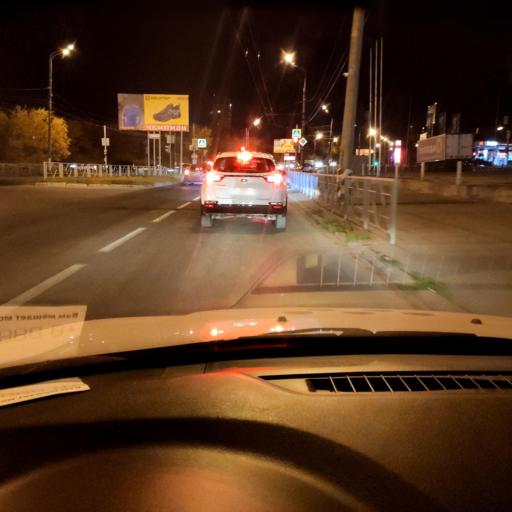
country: RU
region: Samara
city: Tol'yatti
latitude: 53.5079
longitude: 49.2546
